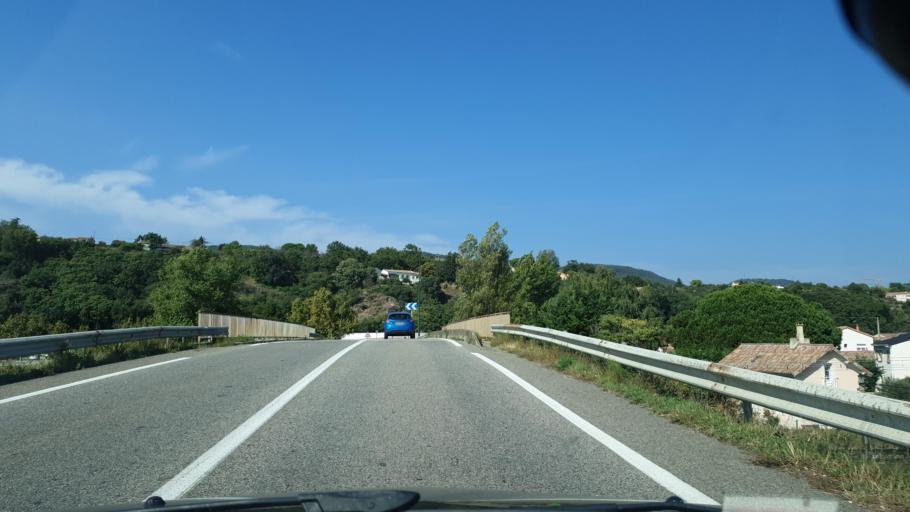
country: FR
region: Rhone-Alpes
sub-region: Departement de l'Ardeche
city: Charmes-sur-Rhone
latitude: 44.8559
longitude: 4.8329
